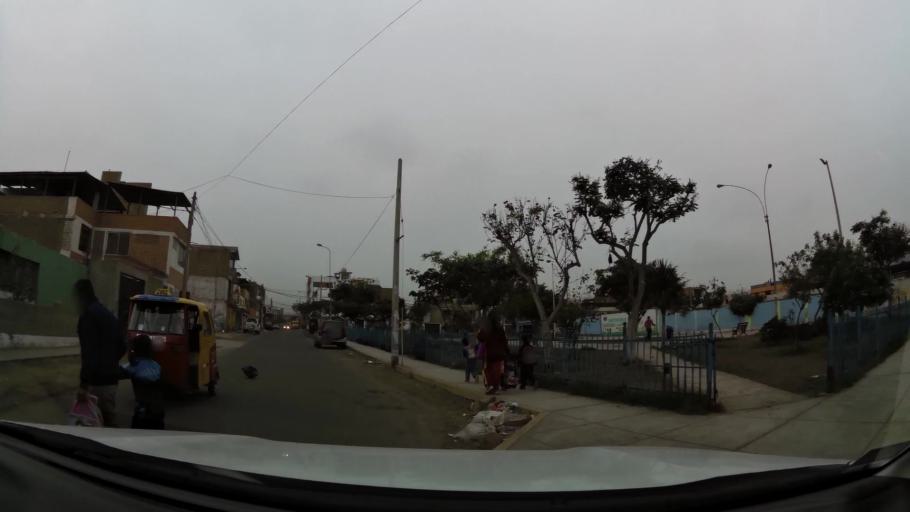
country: PE
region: Lima
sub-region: Lima
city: Surco
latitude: -12.1695
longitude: -76.9751
